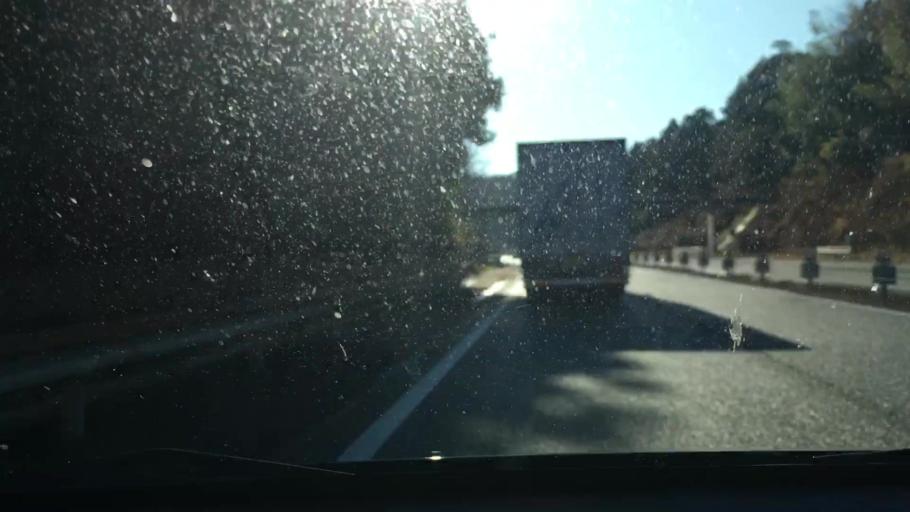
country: JP
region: Kagoshima
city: Kajiki
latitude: 31.8690
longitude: 130.6897
